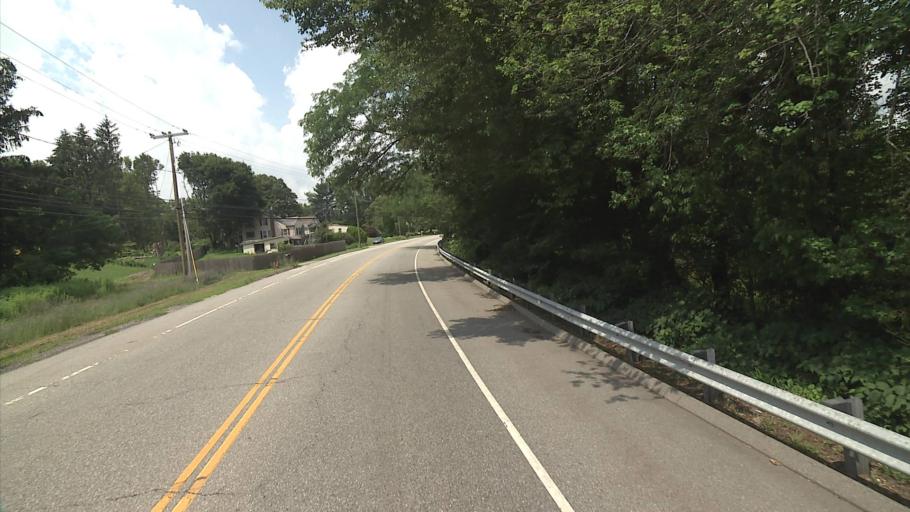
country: US
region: Connecticut
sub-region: New London County
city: Jewett City
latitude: 41.5916
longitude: -71.9635
